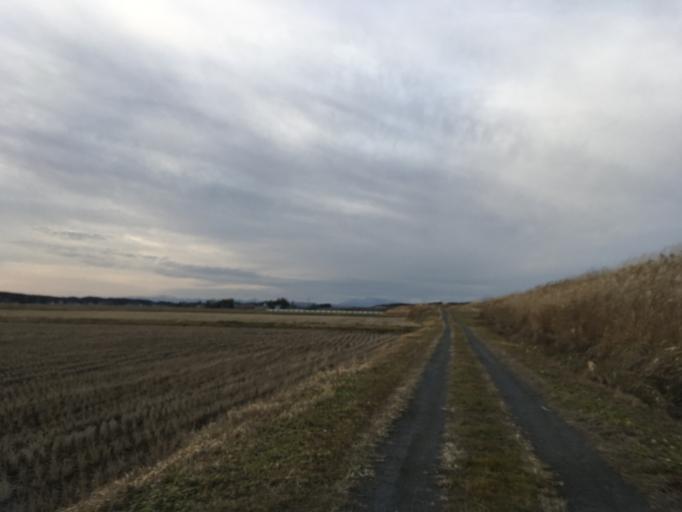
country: JP
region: Miyagi
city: Kogota
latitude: 38.6476
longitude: 141.0663
